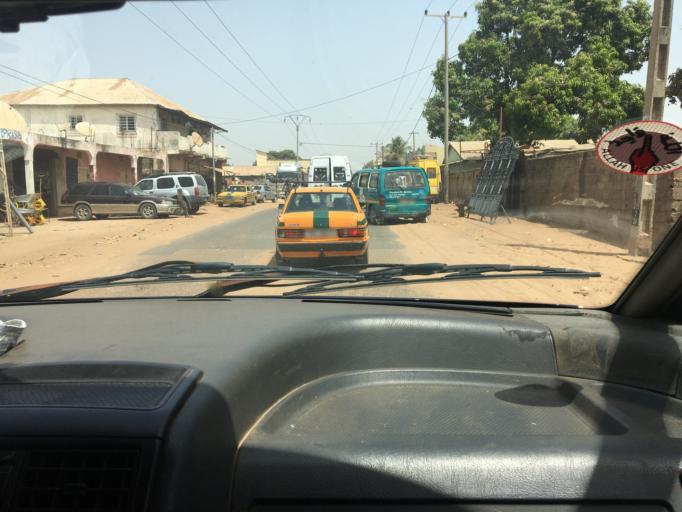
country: GM
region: Western
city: Abuko
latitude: 13.3989
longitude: -16.6733
